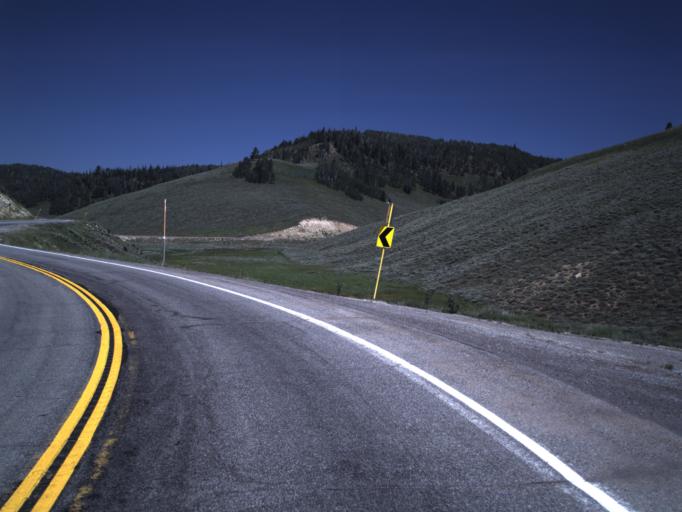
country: US
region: Utah
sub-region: Sanpete County
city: Fairview
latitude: 39.6814
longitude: -111.2433
